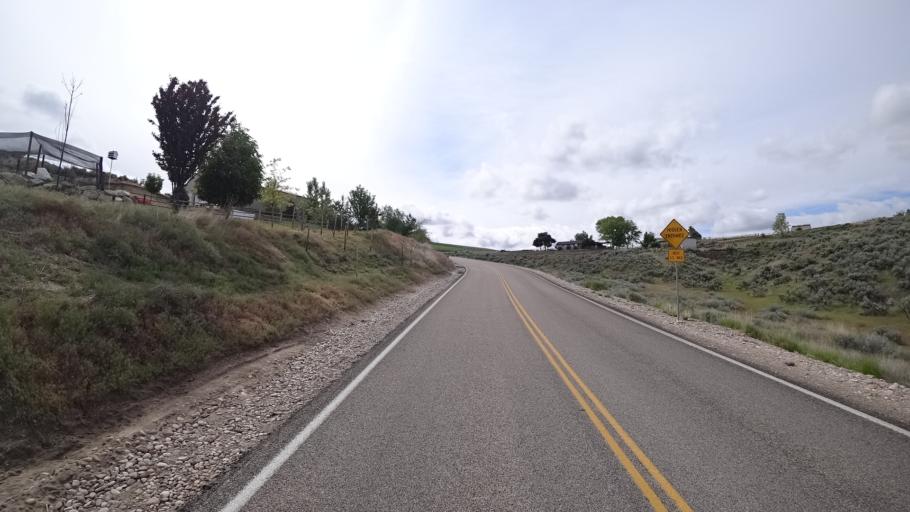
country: US
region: Idaho
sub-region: Ada County
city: Eagle
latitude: 43.7425
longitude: -116.3572
